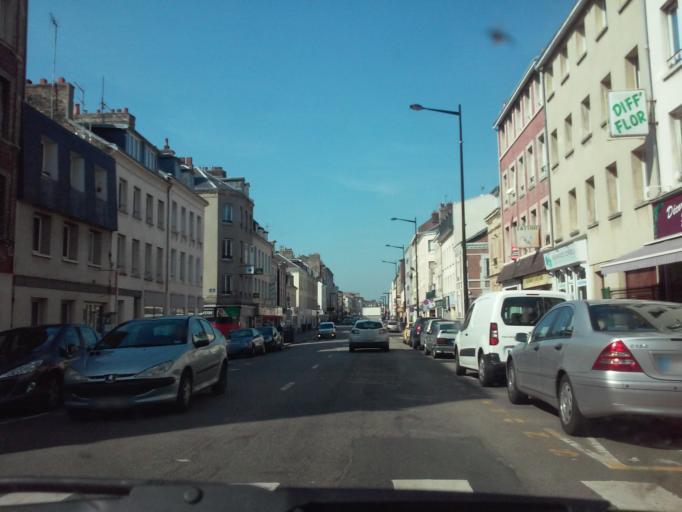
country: FR
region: Haute-Normandie
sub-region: Departement de la Seine-Maritime
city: Le Havre
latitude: 49.5005
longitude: 0.1378
